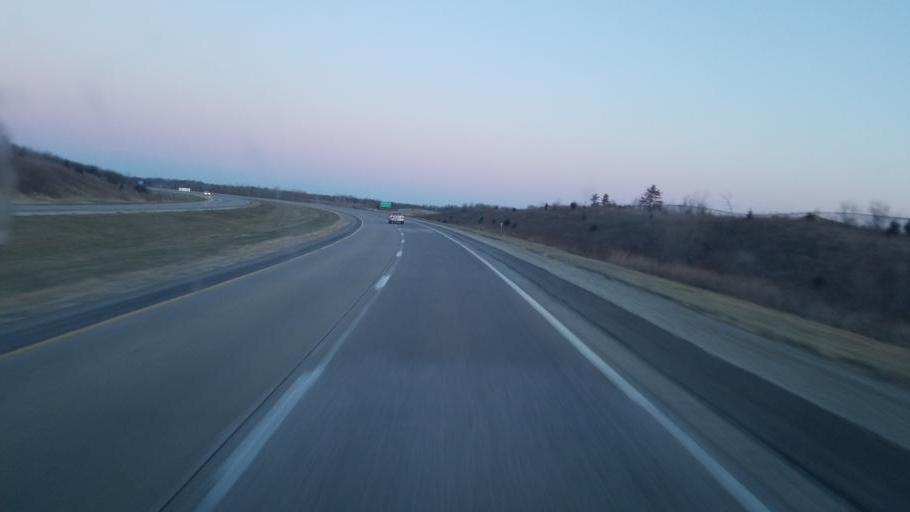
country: US
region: Iowa
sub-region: Henry County
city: Mount Pleasant
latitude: 40.9824
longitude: -91.5168
